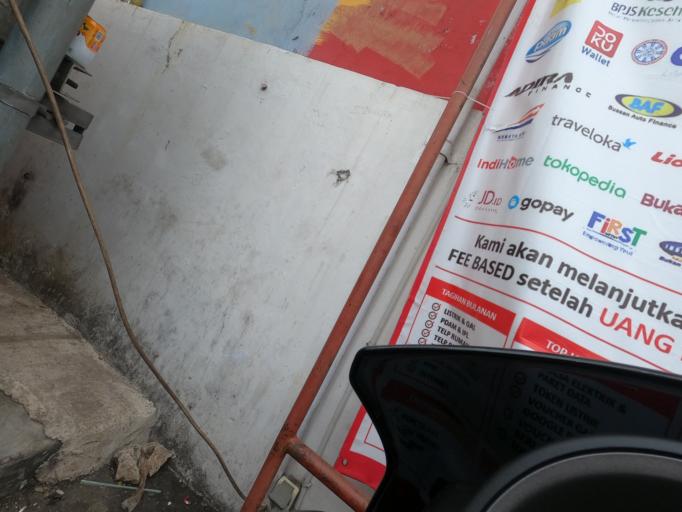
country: ID
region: West Java
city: Lembang
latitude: -6.6775
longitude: 107.6834
